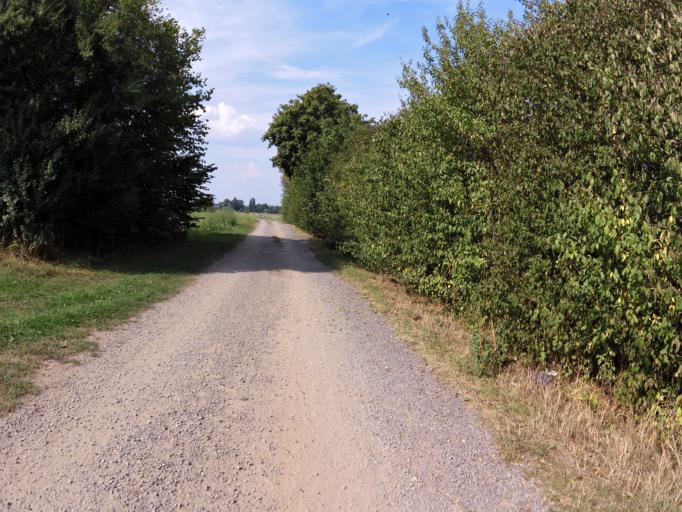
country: DE
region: North Rhine-Westphalia
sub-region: Regierungsbezirk Detmold
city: Petershagen
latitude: 52.3697
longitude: 8.9787
